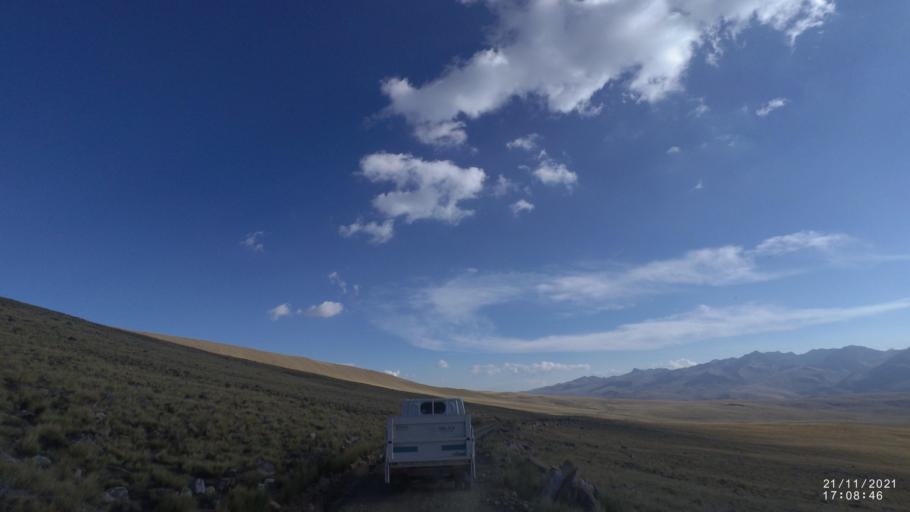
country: BO
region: Cochabamba
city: Cochabamba
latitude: -17.1274
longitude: -66.2575
